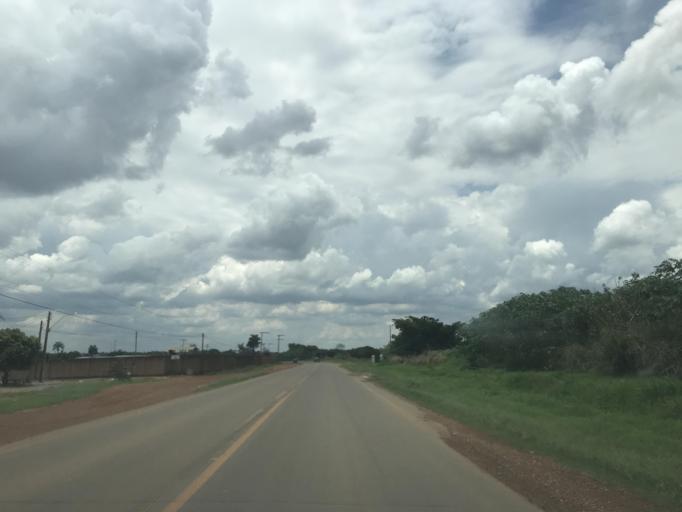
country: BR
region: Goias
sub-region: Vianopolis
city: Vianopolis
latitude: -16.7362
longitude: -48.4935
